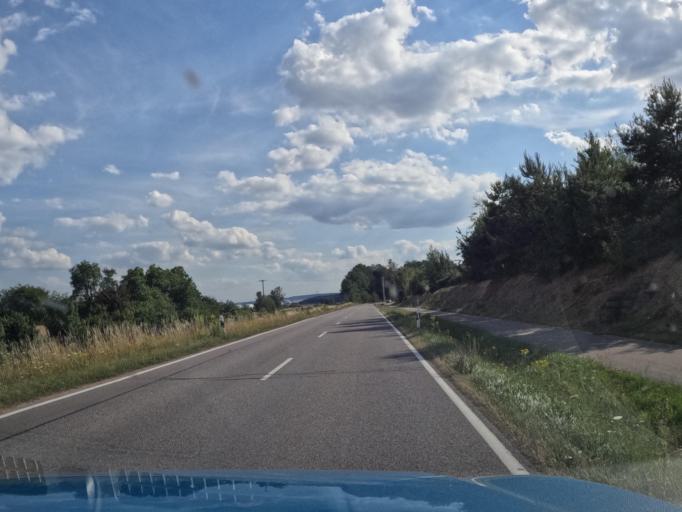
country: DE
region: Bavaria
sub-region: Upper Palatinate
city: Schwarzenfeld
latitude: 49.3851
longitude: 12.1212
